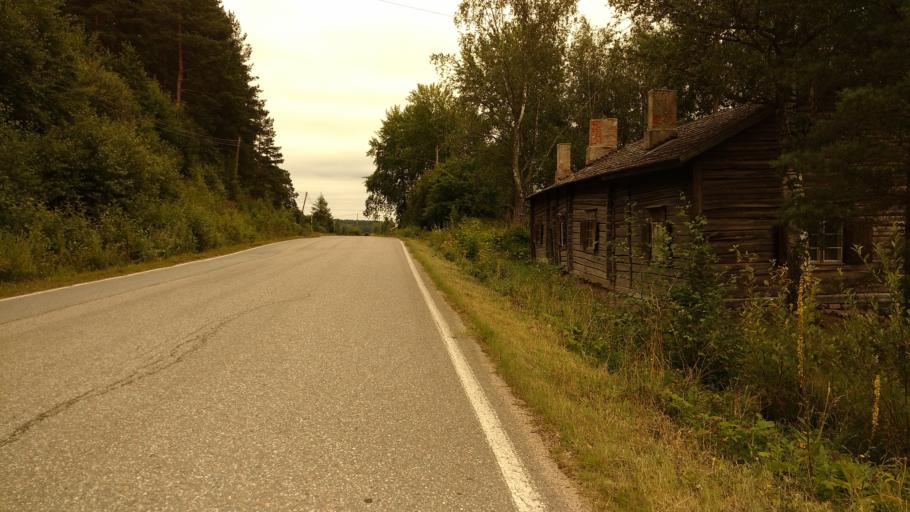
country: FI
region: Varsinais-Suomi
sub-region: Loimaa
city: Marttila
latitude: 60.4151
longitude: 22.8739
